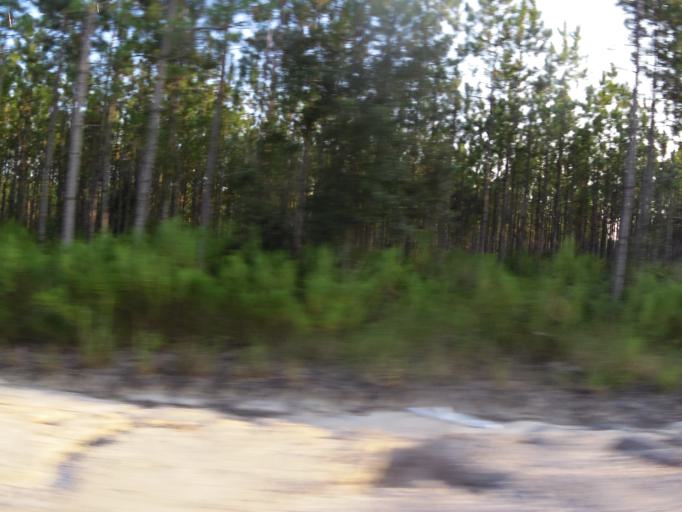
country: US
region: Florida
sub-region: Baker County
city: Macclenny
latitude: 30.3947
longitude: -82.1133
